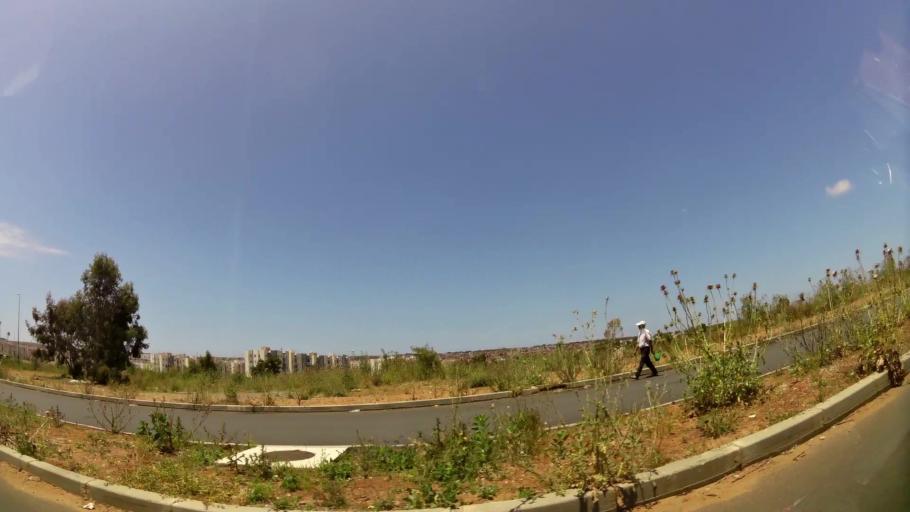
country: MA
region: Gharb-Chrarda-Beni Hssen
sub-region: Kenitra Province
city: Kenitra
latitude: 34.2540
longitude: -6.6317
